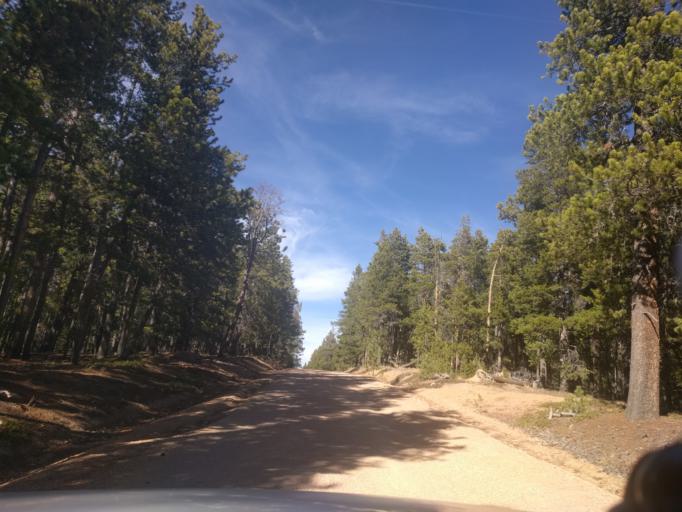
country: US
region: Colorado
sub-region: Douglas County
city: Perry Park
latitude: 39.2164
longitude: -105.0587
